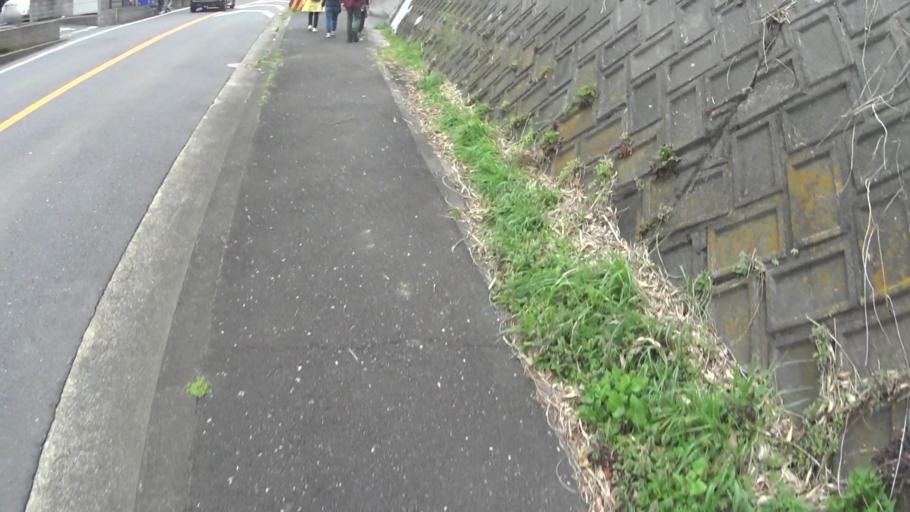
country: JP
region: Kanagawa
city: Fujisawa
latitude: 35.3183
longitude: 139.5000
